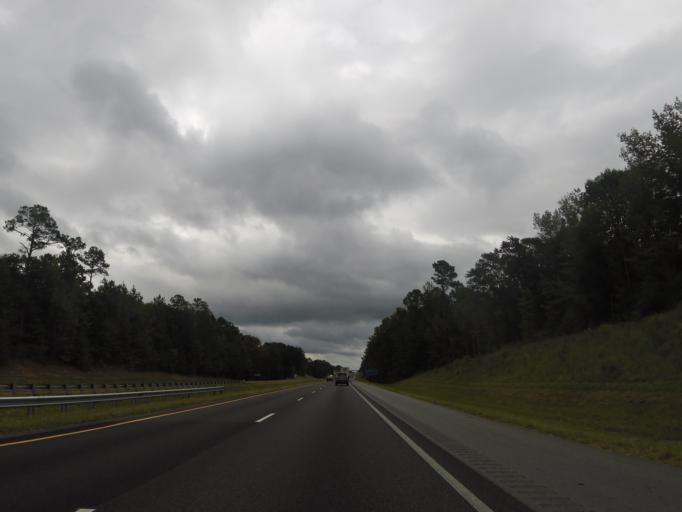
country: US
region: Alabama
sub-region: Conecuh County
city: Evergreen
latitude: 31.4956
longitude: -86.9331
